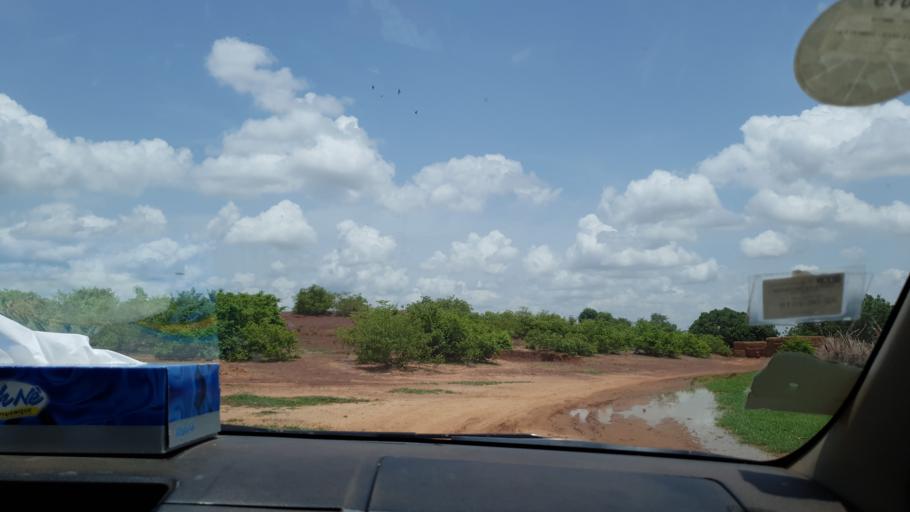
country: ML
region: Koulikoro
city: Banamba
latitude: 13.3756
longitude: -7.2205
